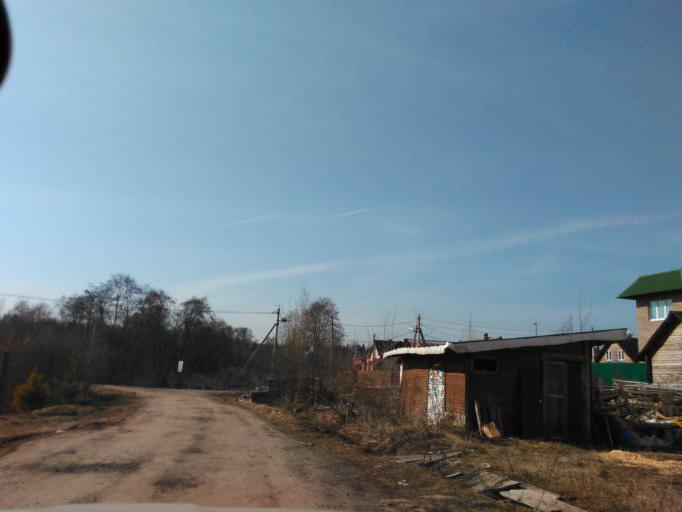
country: RU
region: Moskovskaya
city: Opalikha
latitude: 55.8740
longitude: 37.2511
